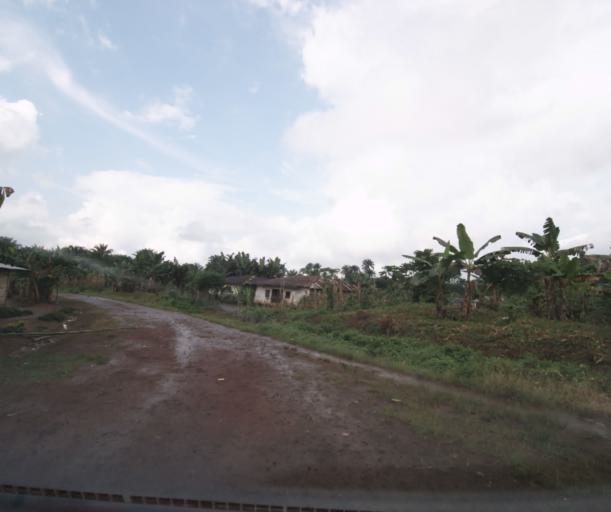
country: CM
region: Littoral
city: Melong
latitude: 5.0575
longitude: 9.9687
